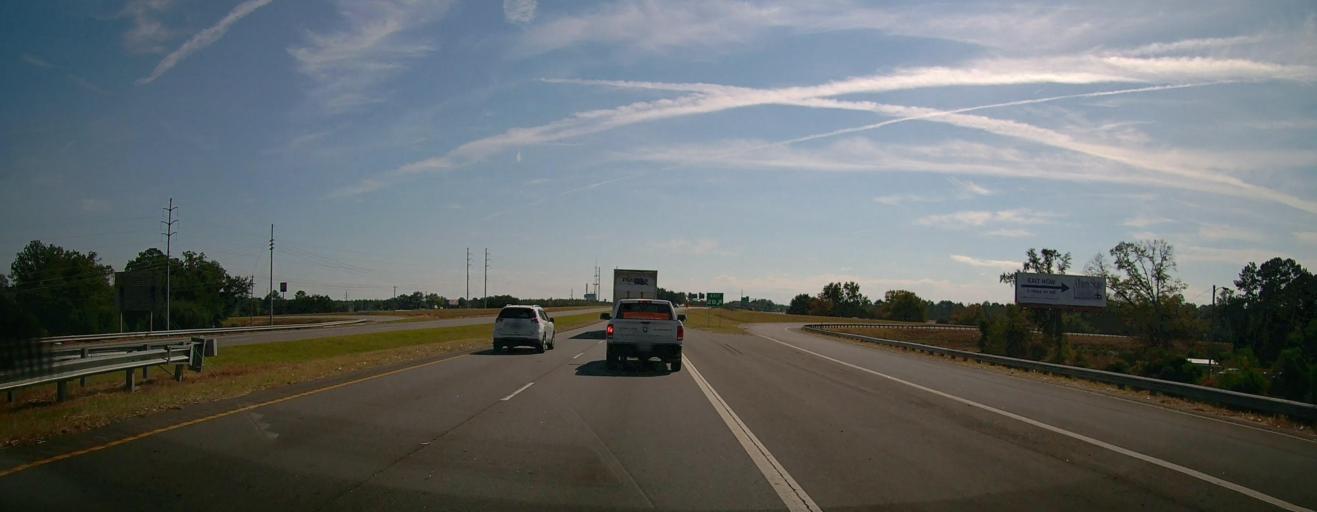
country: US
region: Georgia
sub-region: Dougherty County
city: Albany
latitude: 31.5757
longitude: -84.1115
